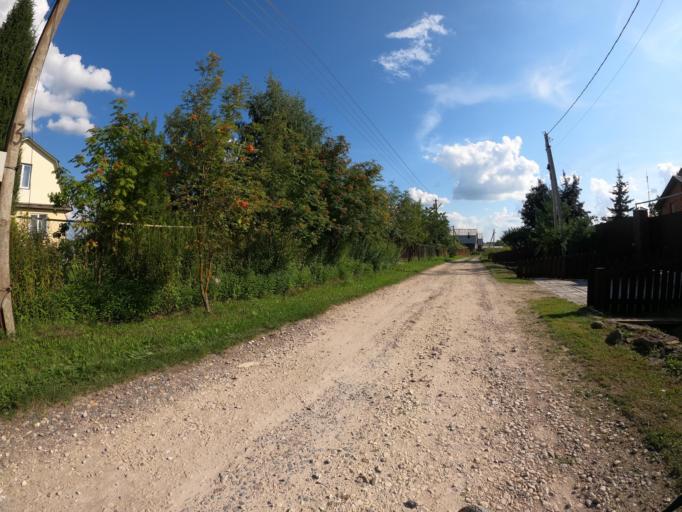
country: RU
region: Moskovskaya
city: Troitskoye
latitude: 55.2336
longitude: 38.4893
